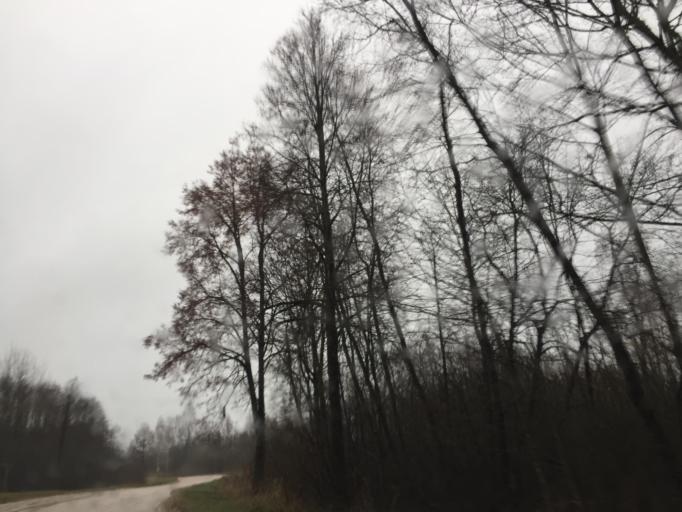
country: LV
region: Viesite
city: Viesite
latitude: 56.4549
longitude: 25.4926
